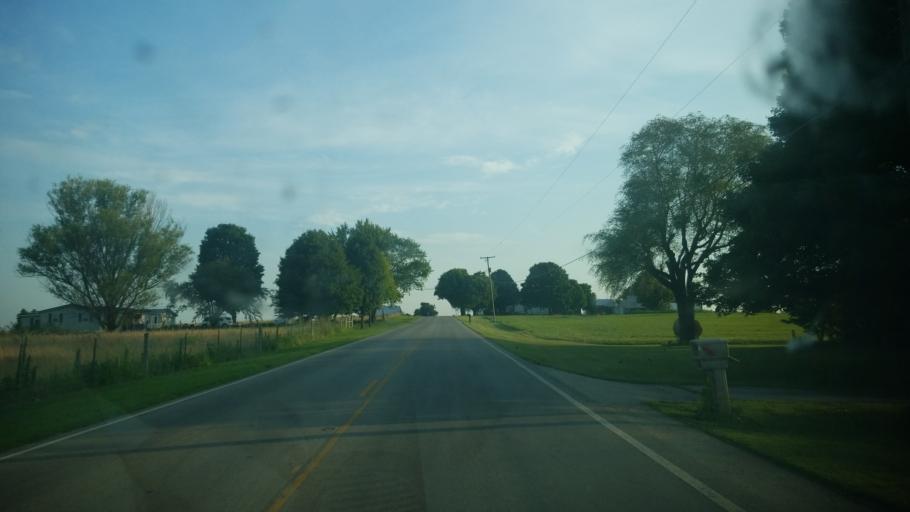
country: US
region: Ohio
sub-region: Adams County
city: Peebles
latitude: 38.9258
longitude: -83.4230
